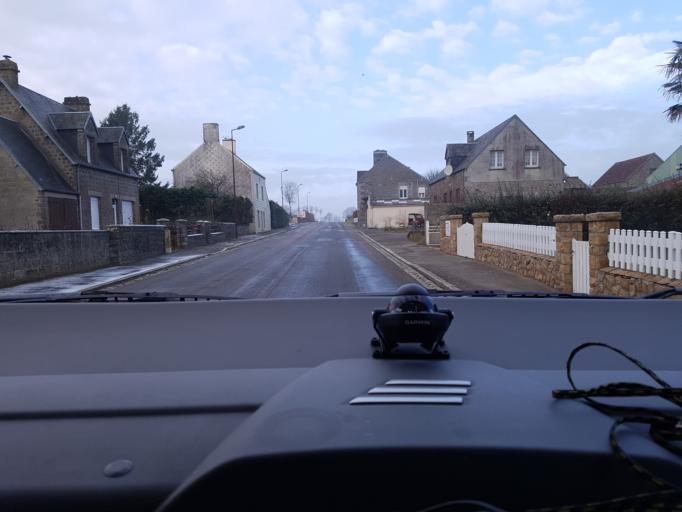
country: FR
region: Lower Normandy
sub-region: Departement de la Manche
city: Sourdeval
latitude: 48.7652
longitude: -0.9778
